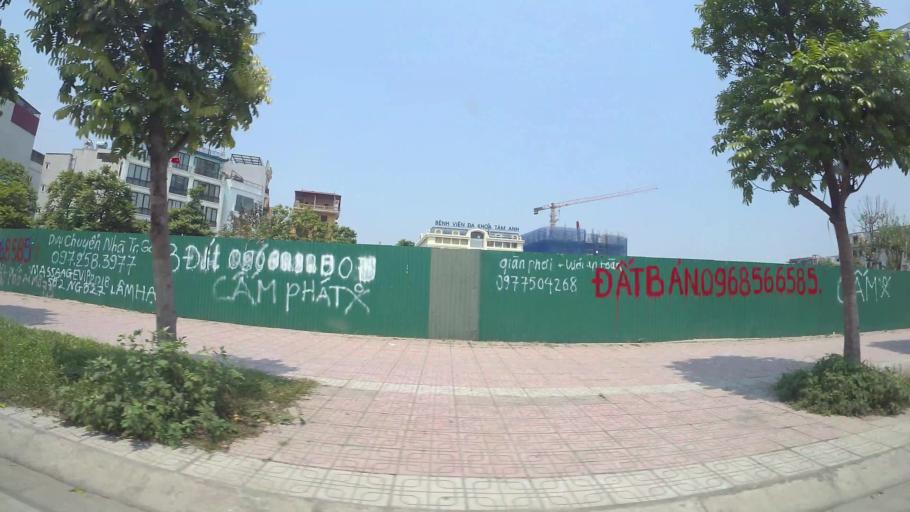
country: VN
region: Ha Noi
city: Hoan Kiem
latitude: 21.0398
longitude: 105.8751
